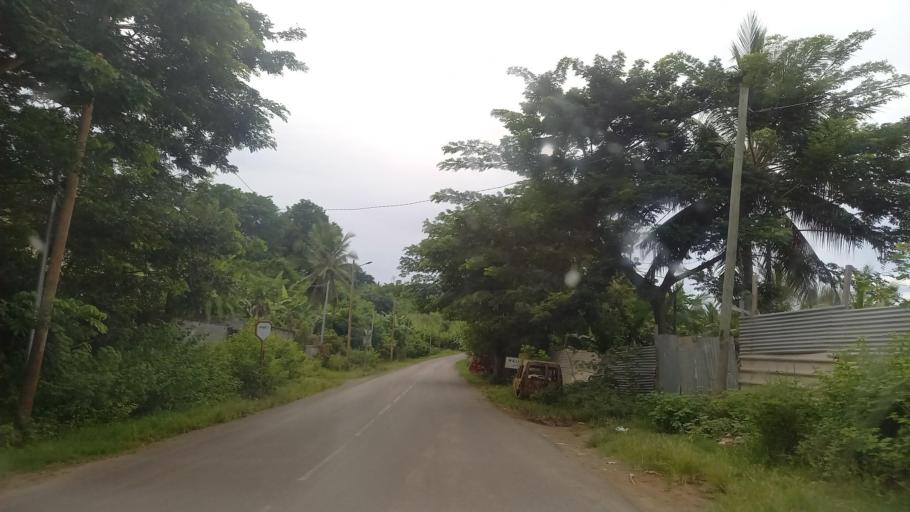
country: YT
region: Kani-Keli
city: Kani Keli
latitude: -12.9250
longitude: 45.1061
